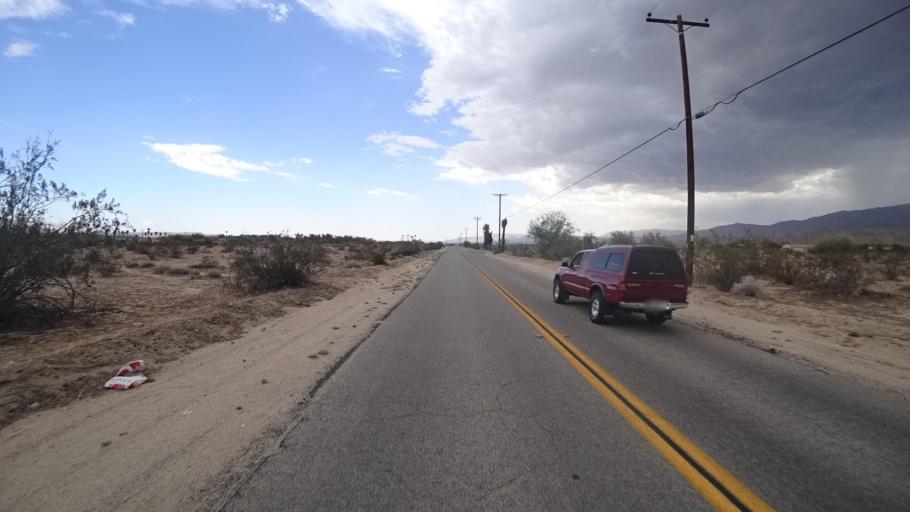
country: US
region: California
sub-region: San Diego County
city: Borrego Springs
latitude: 33.2745
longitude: -116.3892
